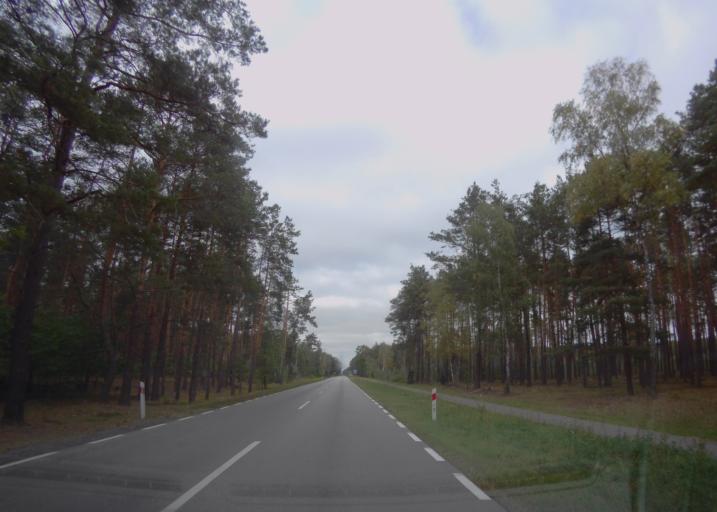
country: PL
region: Lublin Voivodeship
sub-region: Powiat wlodawski
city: Wlodawa
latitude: 51.4869
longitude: 23.5169
